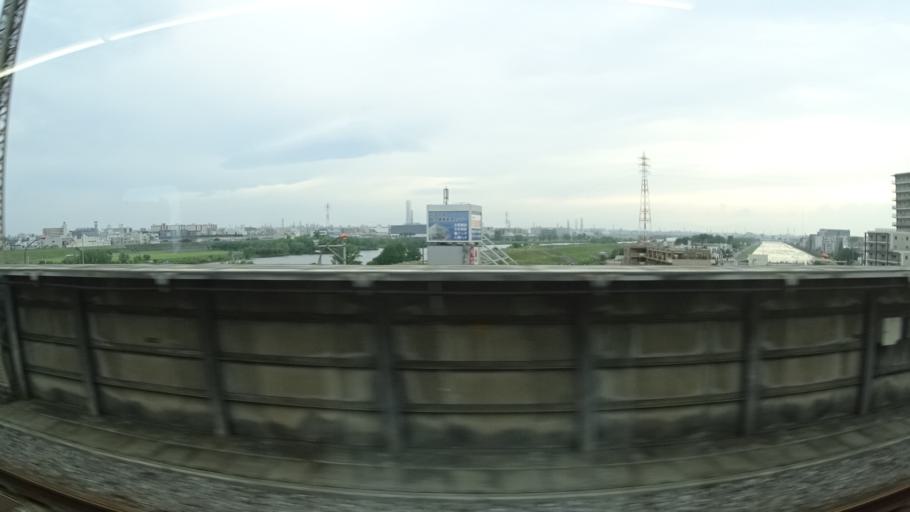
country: JP
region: Saitama
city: Shimotoda
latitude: 35.8022
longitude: 139.6841
